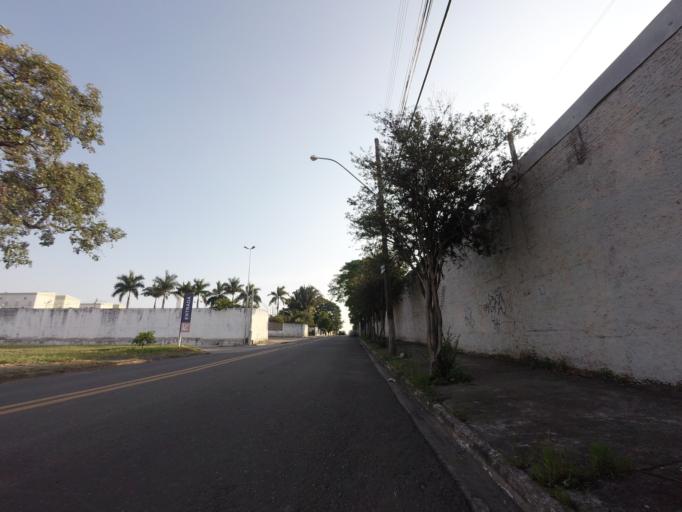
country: BR
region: Sao Paulo
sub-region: Piracicaba
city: Piracicaba
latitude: -22.7357
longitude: -47.6082
